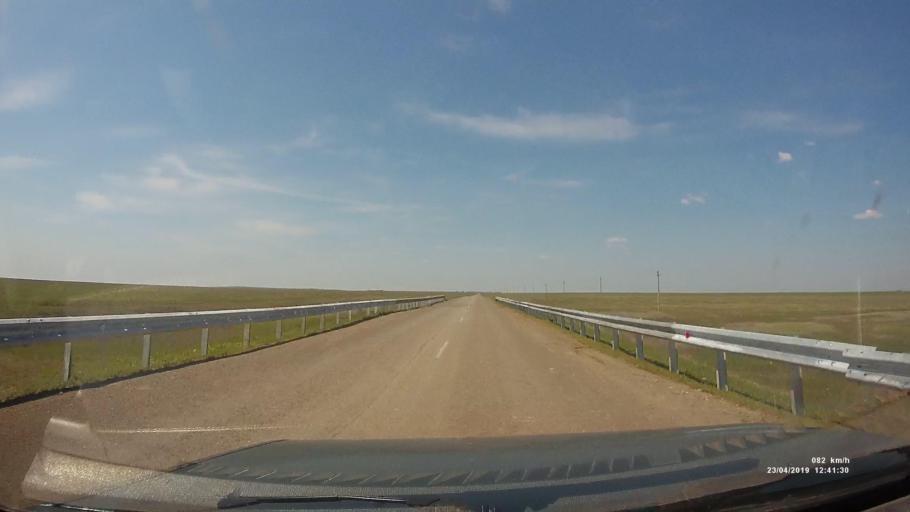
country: RU
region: Kalmykiya
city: Yashalta
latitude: 46.4490
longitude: 42.6790
